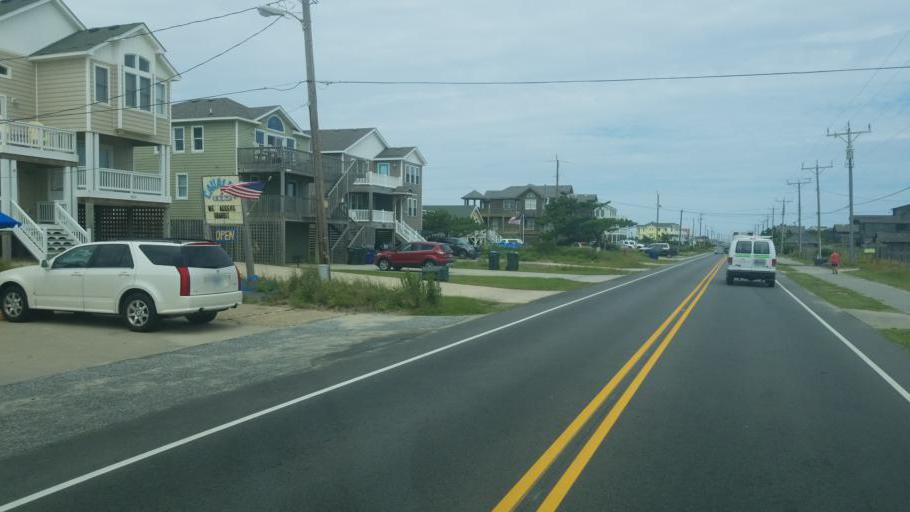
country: US
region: North Carolina
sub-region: Dare County
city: Nags Head
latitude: 35.9487
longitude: -75.6193
